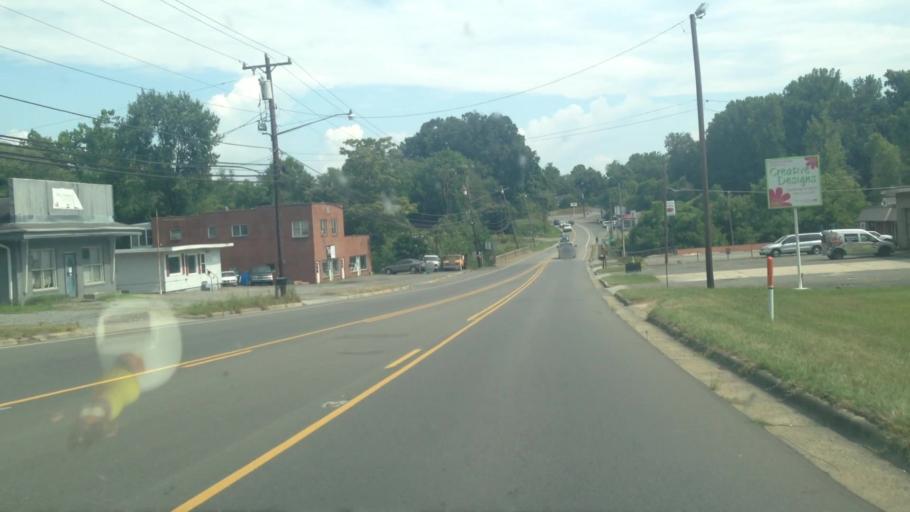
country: US
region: North Carolina
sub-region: Surry County
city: Mount Airy
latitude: 36.4924
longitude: -80.5960
